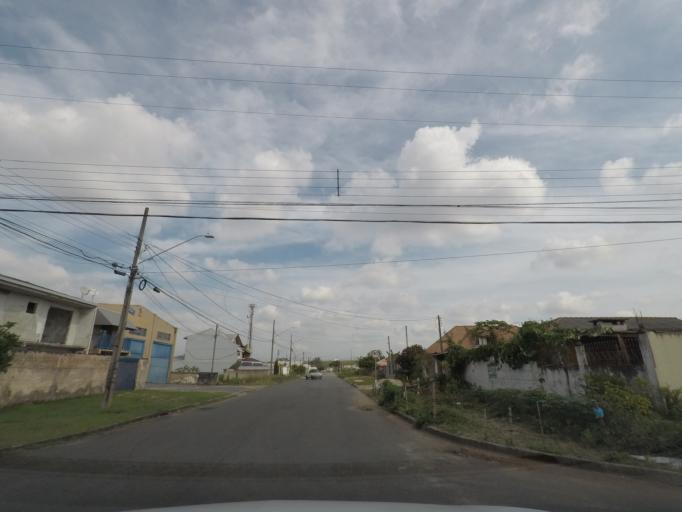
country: BR
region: Parana
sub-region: Pinhais
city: Pinhais
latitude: -25.4768
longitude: -49.1967
